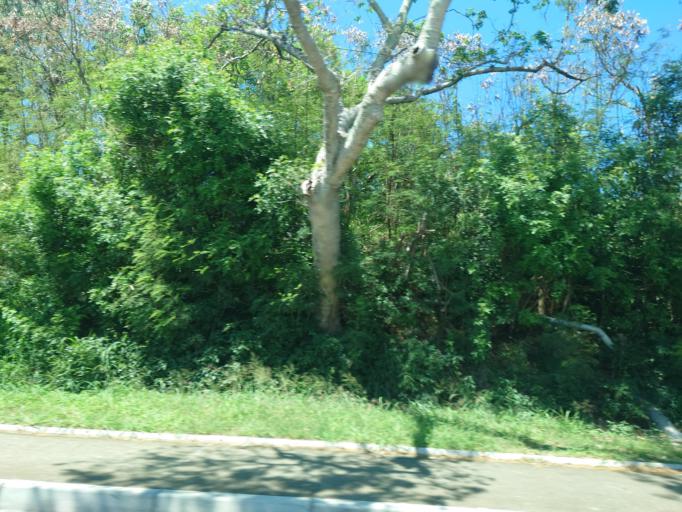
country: NC
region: South Province
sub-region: Noumea
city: Noumea
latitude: -22.2686
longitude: 166.4591
